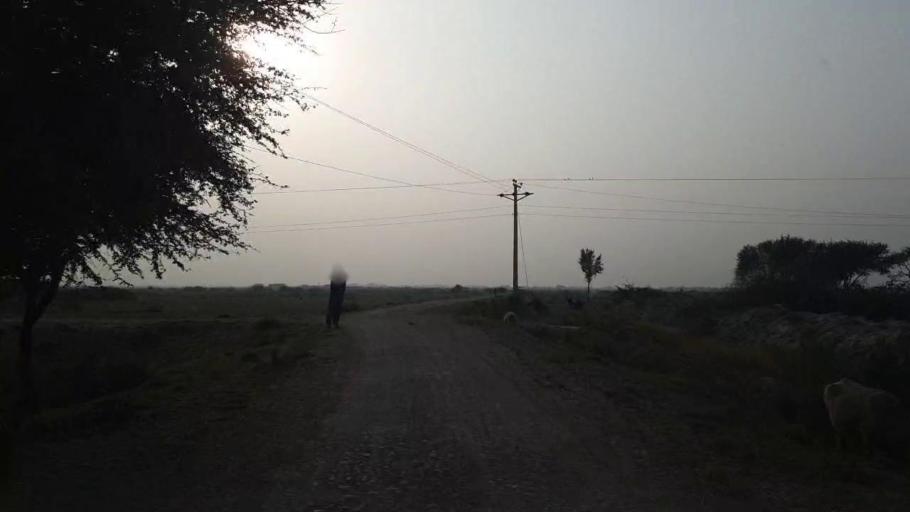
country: PK
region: Sindh
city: Mirpur Batoro
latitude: 24.6605
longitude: 68.3755
